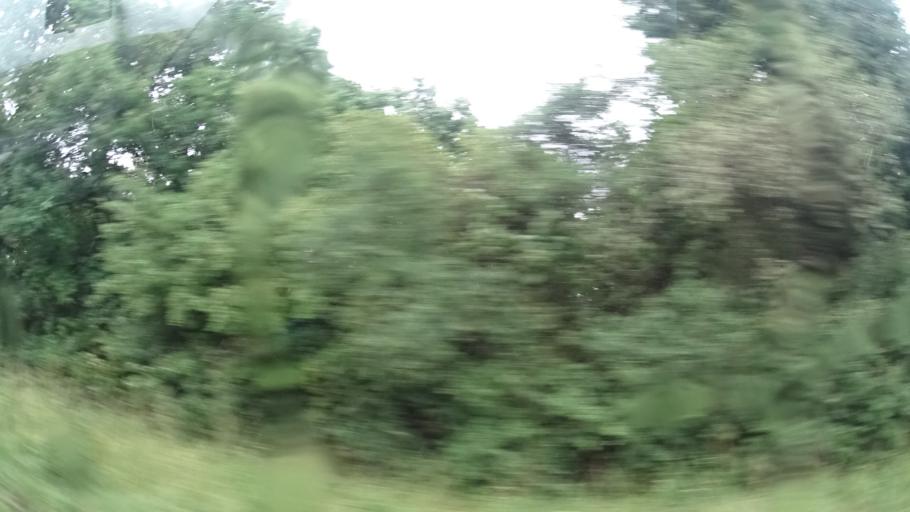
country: LU
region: Grevenmacher
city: Schengen
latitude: 49.4717
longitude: 6.3360
